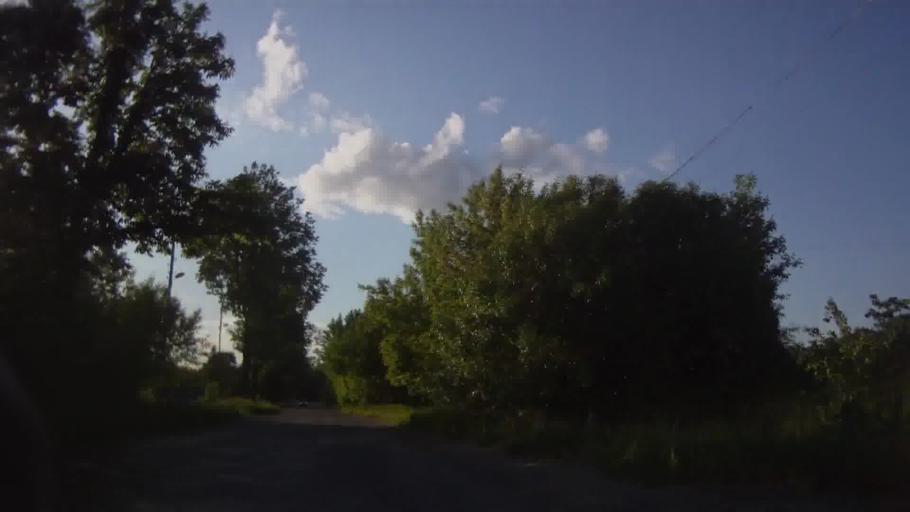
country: LV
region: Rezekne
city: Rezekne
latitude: 56.5292
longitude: 27.3167
